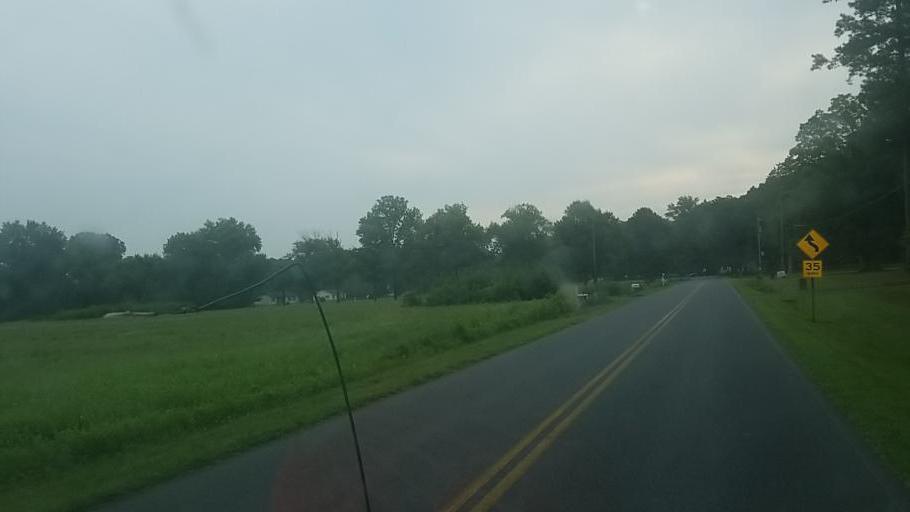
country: US
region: Maryland
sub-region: Wicomico County
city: Delmar
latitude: 38.4134
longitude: -75.5128
